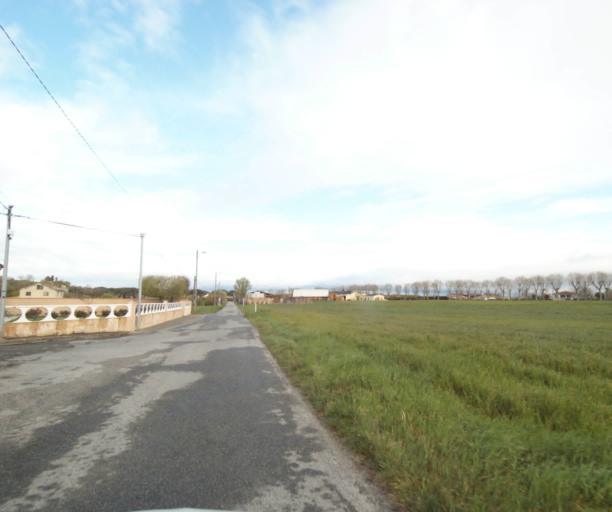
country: FR
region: Midi-Pyrenees
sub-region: Departement de l'Ariege
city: Saverdun
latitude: 43.2297
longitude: 1.5879
